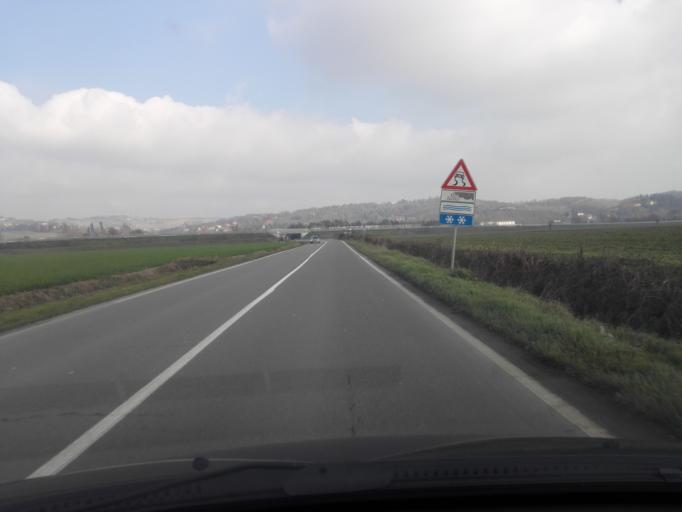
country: IT
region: Piedmont
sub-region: Provincia di Alessandria
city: Valle San Bartolomeo
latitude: 44.9419
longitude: 8.6330
